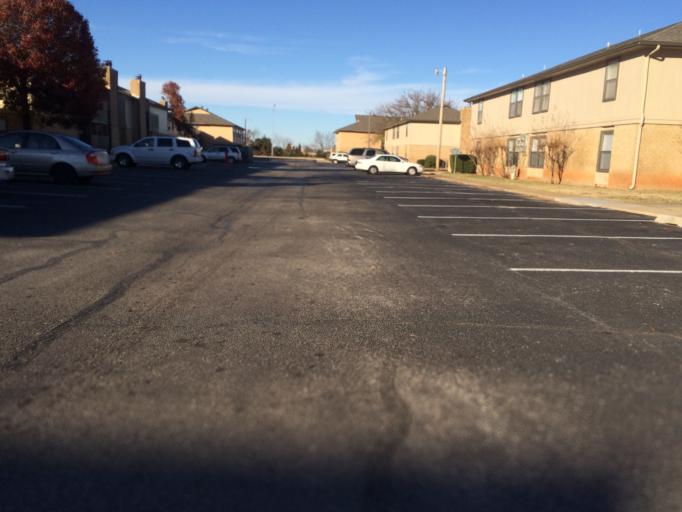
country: US
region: Oklahoma
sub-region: Cleveland County
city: Norman
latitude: 35.2316
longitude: -97.4679
